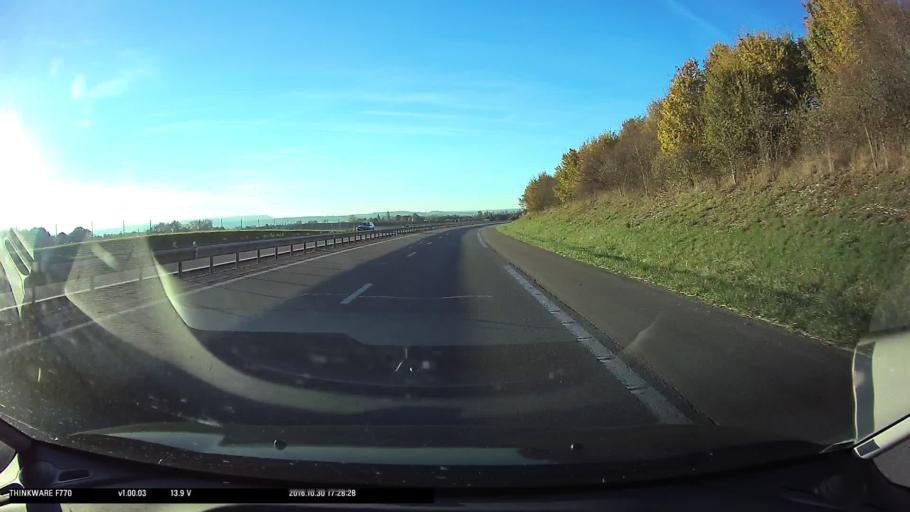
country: FR
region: Bourgogne
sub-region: Departement de la Cote-d'Or
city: Sennecey-les-Dijon
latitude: 47.2869
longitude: 5.0956
